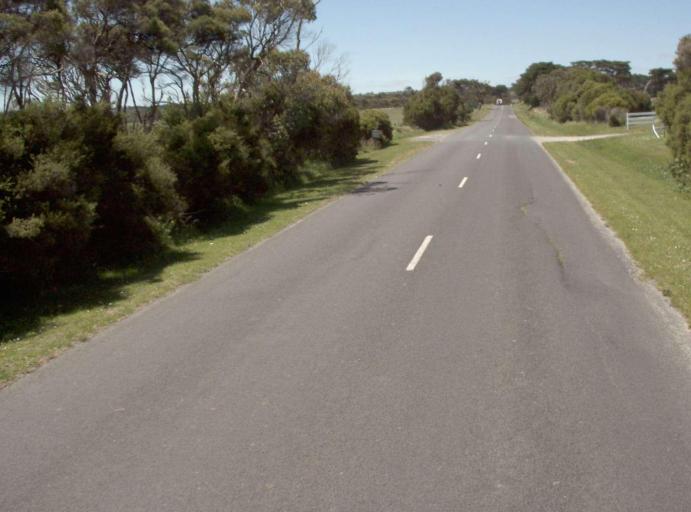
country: AU
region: Victoria
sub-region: Bass Coast
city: North Wonthaggi
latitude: -38.7995
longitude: 146.0861
